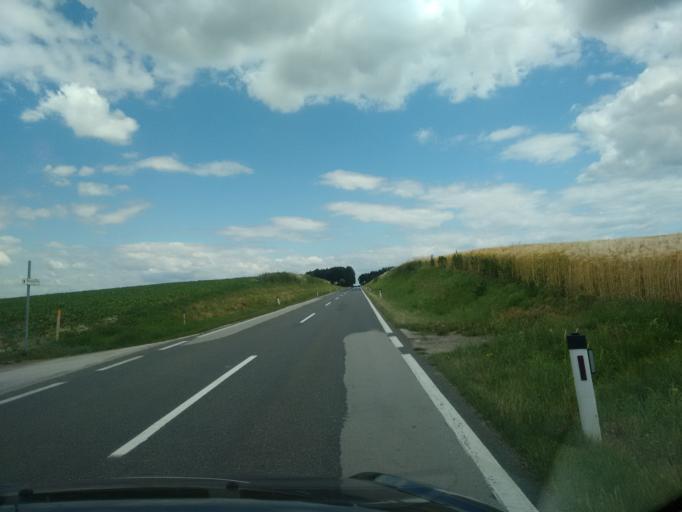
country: AT
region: Upper Austria
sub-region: Politischer Bezirk Steyr-Land
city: Sierning
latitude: 48.1116
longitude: 14.3250
